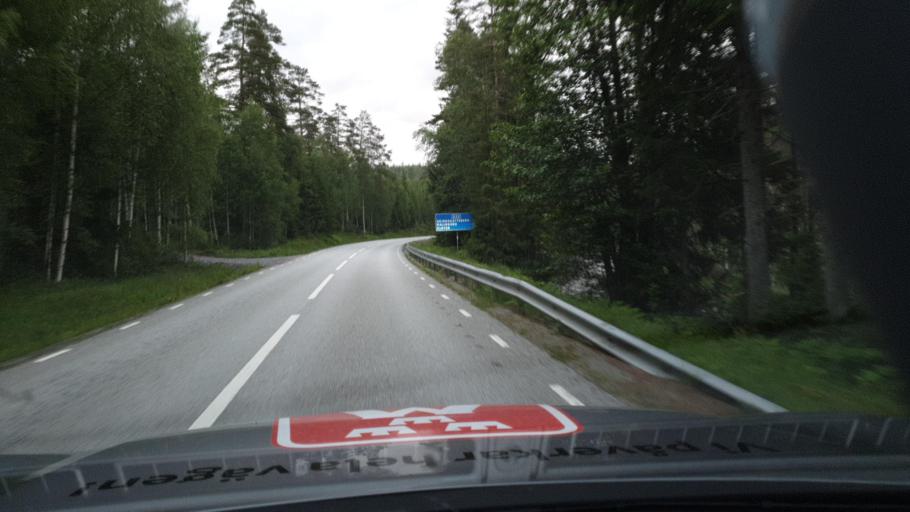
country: SE
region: OErebro
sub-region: Ljusnarsbergs Kommun
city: Kopparberg
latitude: 59.8797
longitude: 15.1399
